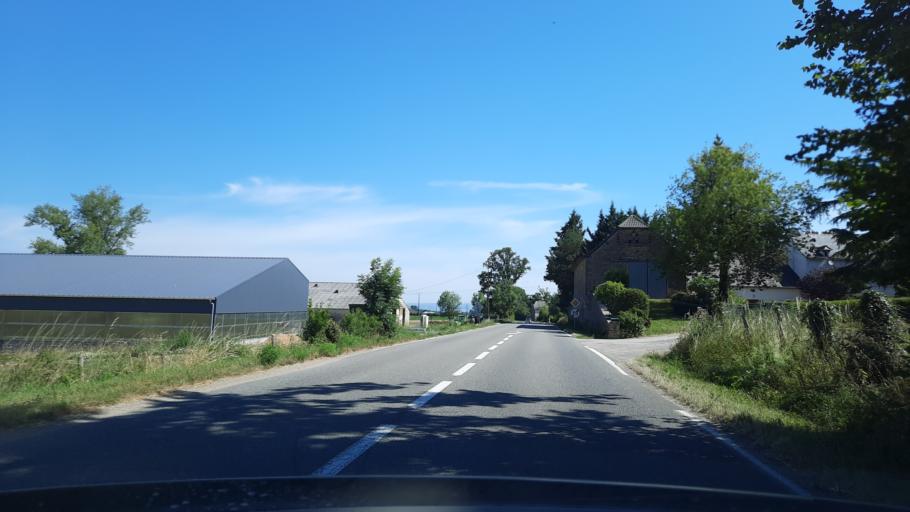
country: FR
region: Midi-Pyrenees
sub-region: Departement de l'Aveyron
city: Montbazens
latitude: 44.4344
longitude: 2.1943
